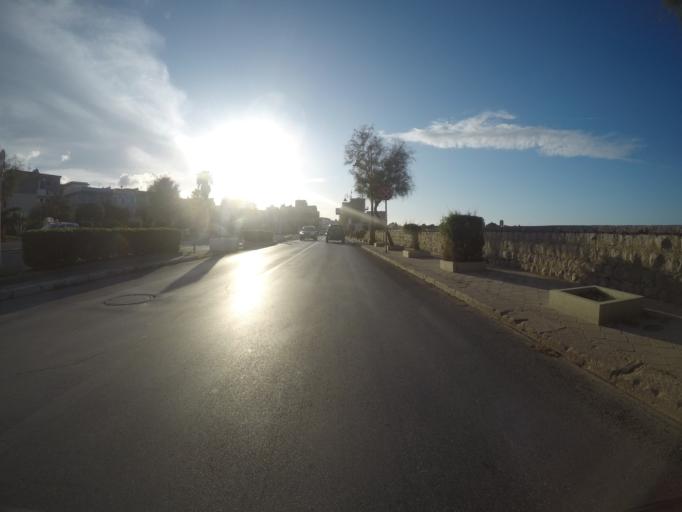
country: IT
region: Sicily
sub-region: Palermo
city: Isola delle Femmine
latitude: 38.1986
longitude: 13.2516
